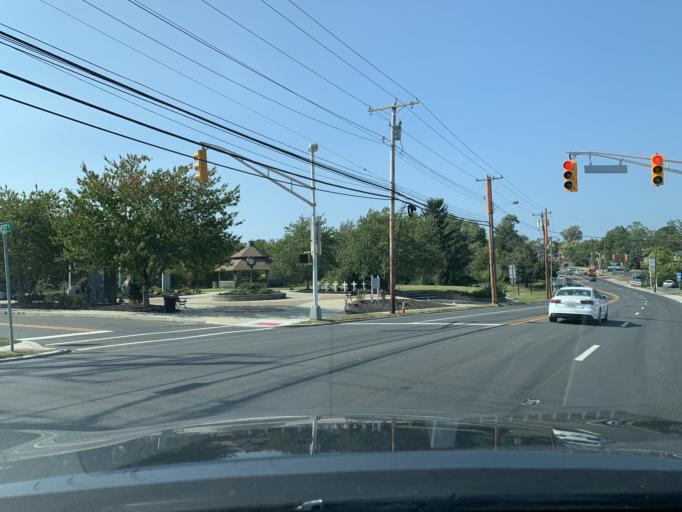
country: US
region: New Jersey
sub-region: Monmouth County
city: Eatontown
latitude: 40.3056
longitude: -74.0605
